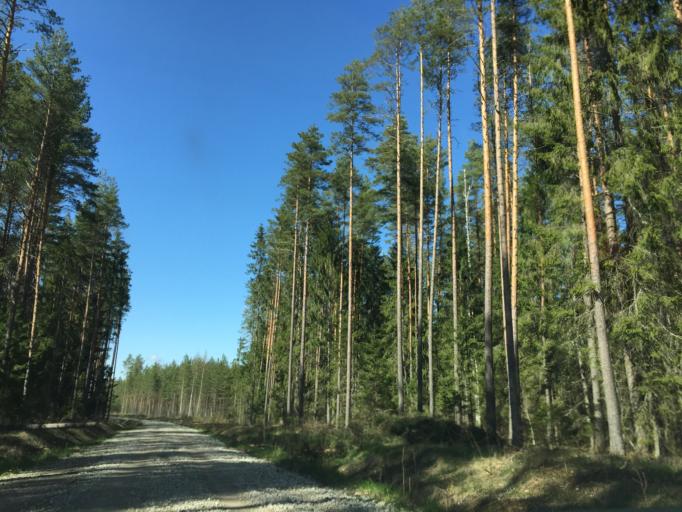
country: LV
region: Strenci
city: Strenci
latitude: 57.5959
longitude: 25.6911
